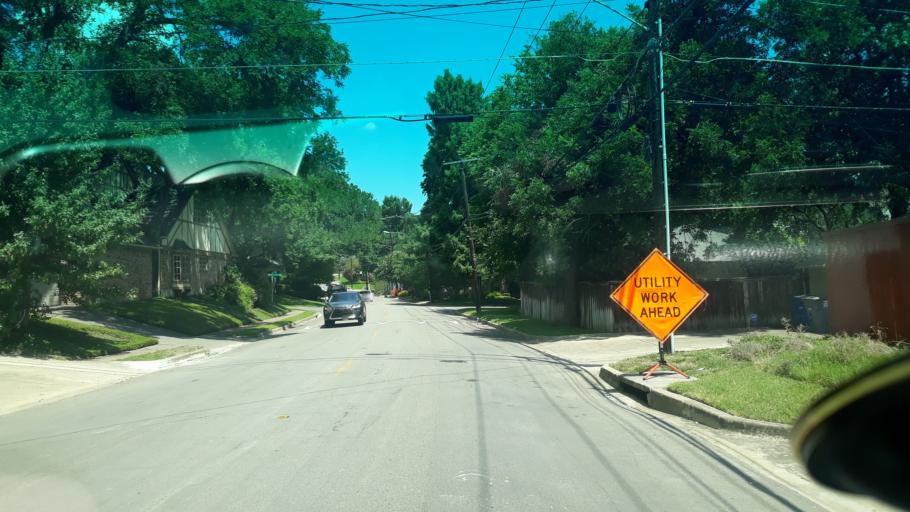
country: US
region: Texas
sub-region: Dallas County
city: Highland Park
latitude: 32.8165
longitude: -96.7372
